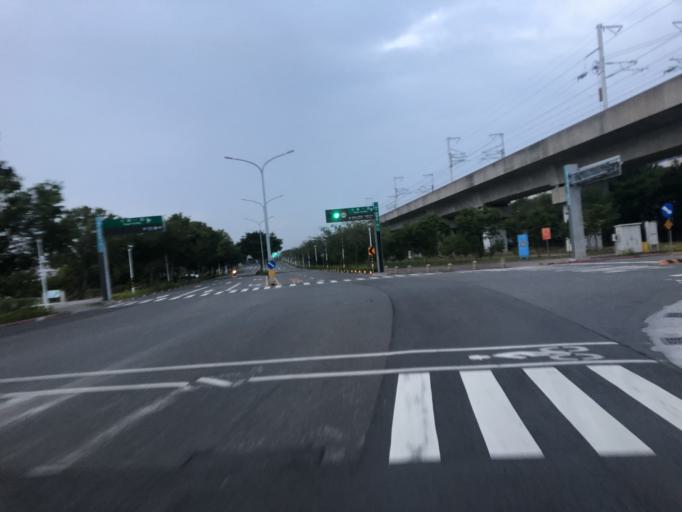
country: TW
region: Taiwan
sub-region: Tainan
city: Tainan
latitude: 23.0872
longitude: 120.2864
